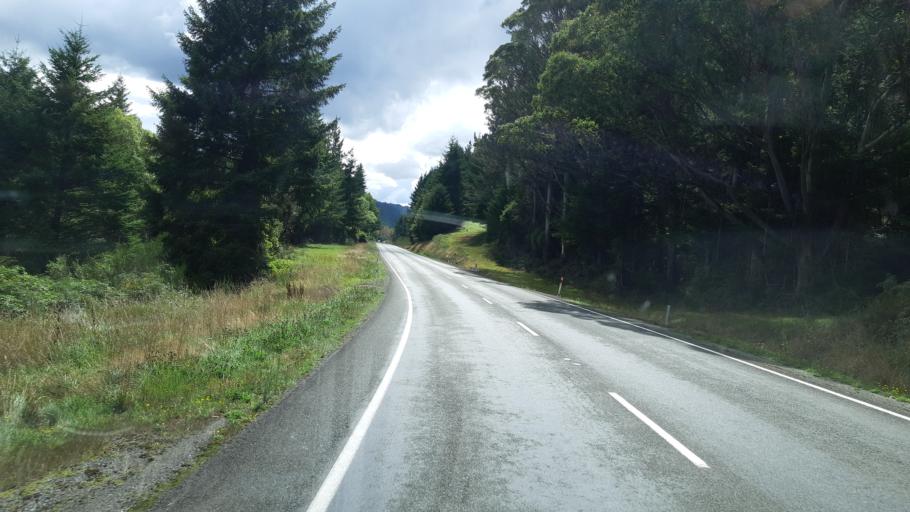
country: NZ
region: Tasman
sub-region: Tasman District
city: Wakefield
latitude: -41.5963
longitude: 172.7628
